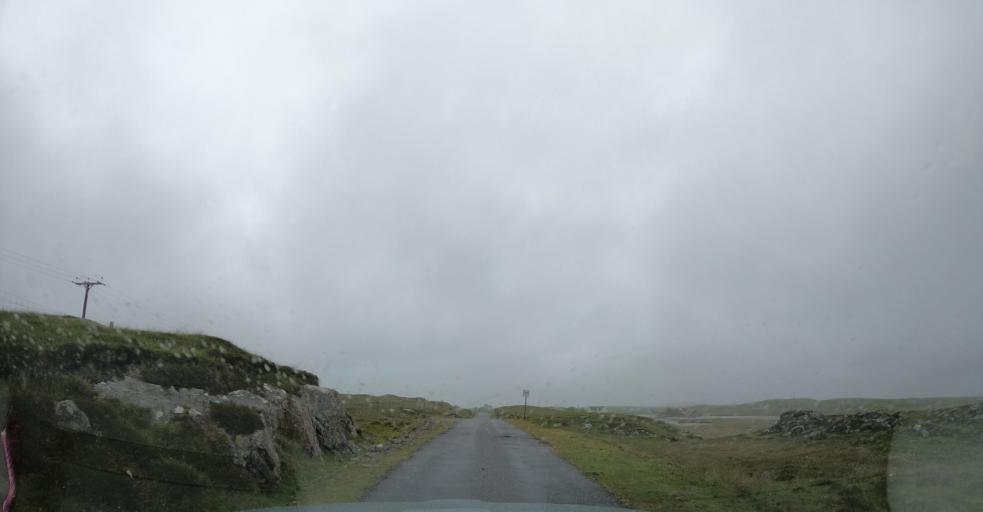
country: GB
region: Scotland
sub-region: Eilean Siar
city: Benbecula
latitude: 57.4976
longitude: -7.2416
